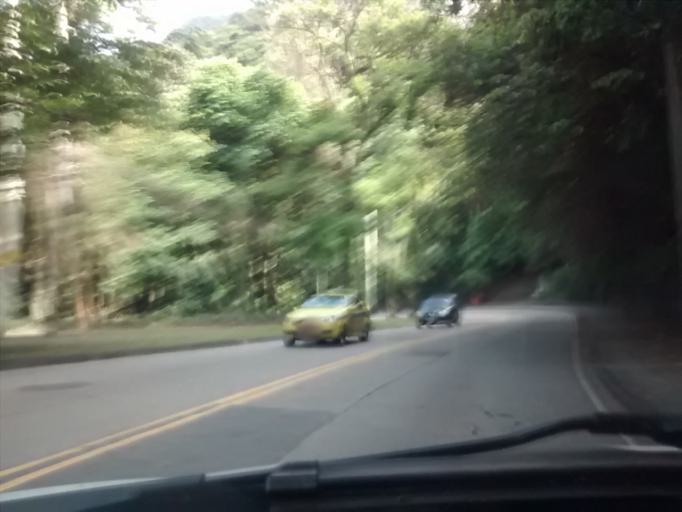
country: BR
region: Rio de Janeiro
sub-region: Rio De Janeiro
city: Rio de Janeiro
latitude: -22.9579
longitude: -43.2657
